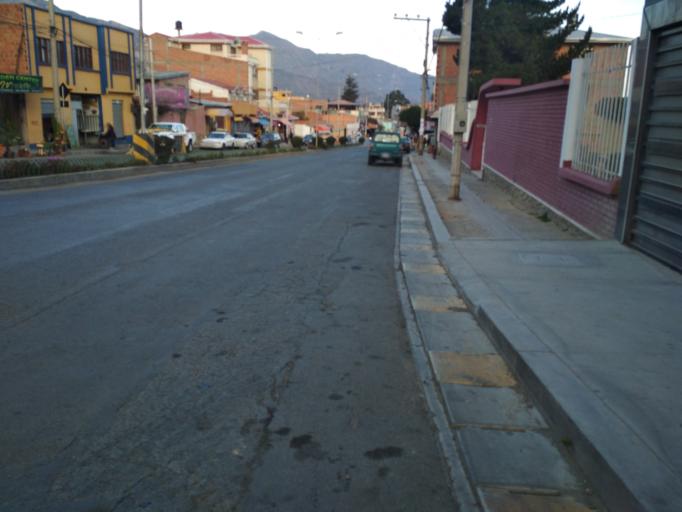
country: BO
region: La Paz
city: La Paz
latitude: -16.5681
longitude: -68.0880
